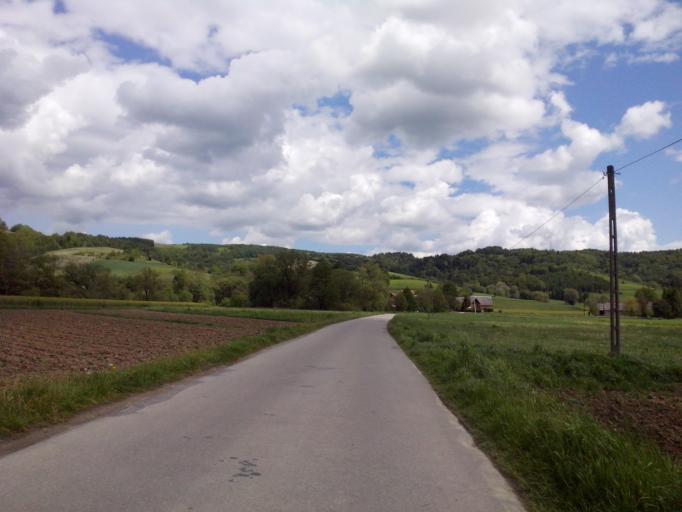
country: PL
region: Subcarpathian Voivodeship
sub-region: Powiat strzyzowski
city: Strzyzow
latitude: 49.8355
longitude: 21.8306
